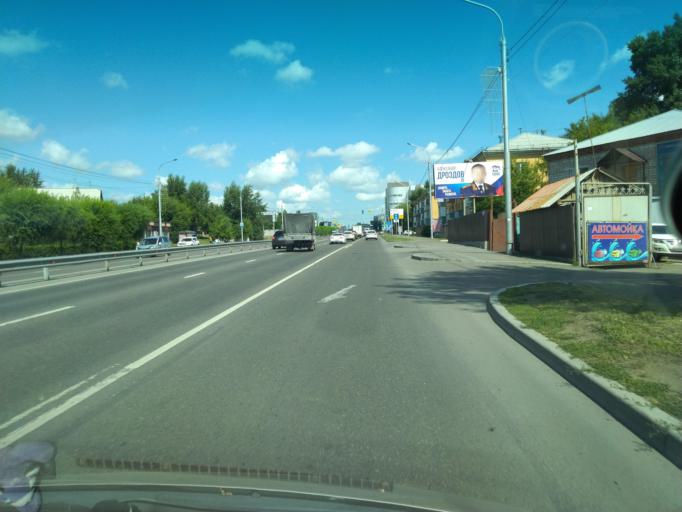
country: RU
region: Krasnoyarskiy
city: Krasnoyarsk
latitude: 56.0261
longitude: 92.8871
